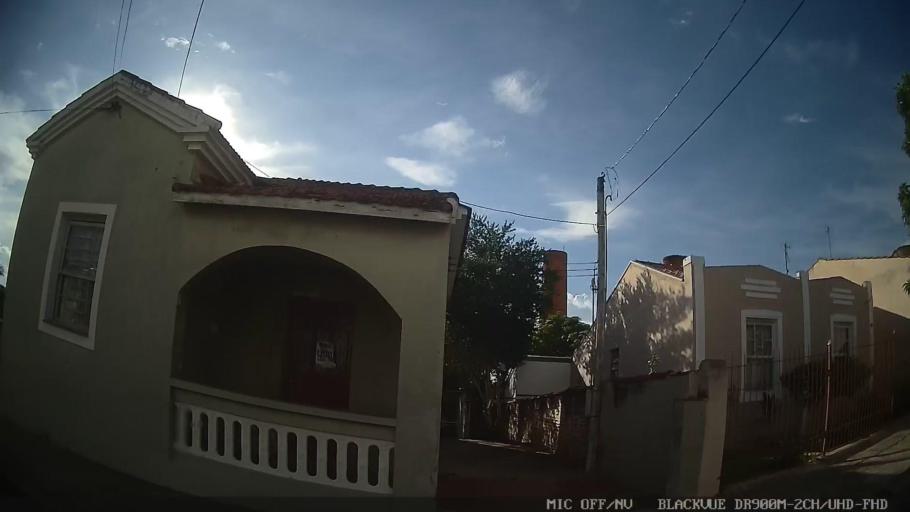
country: BR
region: Sao Paulo
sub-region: Tiete
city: Tiete
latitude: -23.1074
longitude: -47.7157
